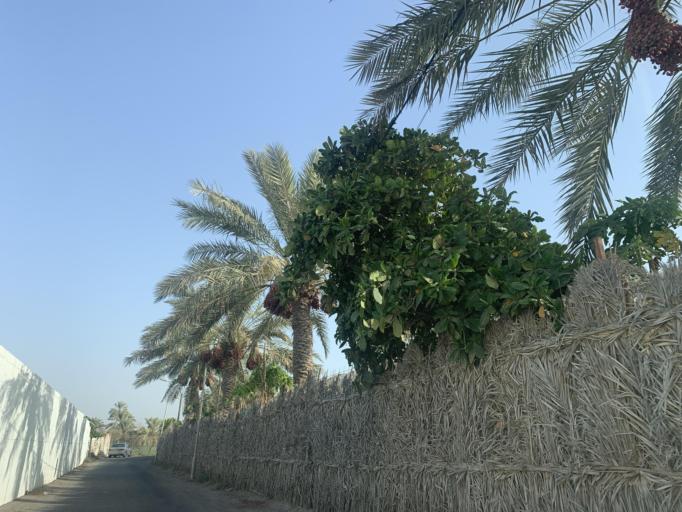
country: BH
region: Central Governorate
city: Madinat Hamad
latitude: 26.1889
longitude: 50.4618
